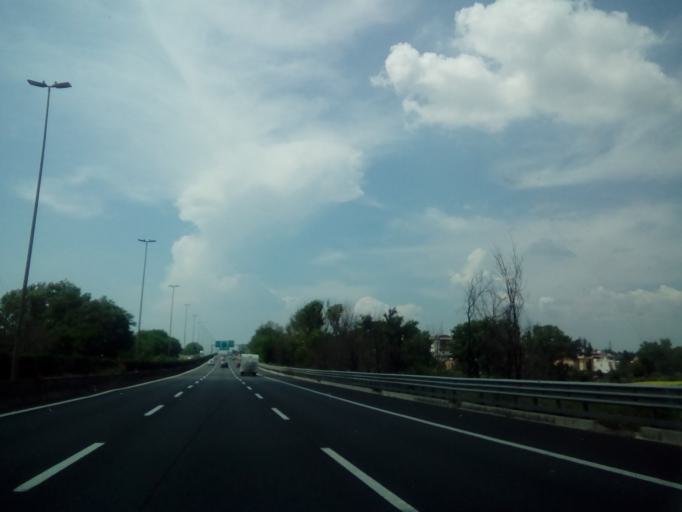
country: IT
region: Latium
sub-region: Citta metropolitana di Roma Capitale
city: Colle Verde
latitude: 41.9682
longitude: 12.5594
